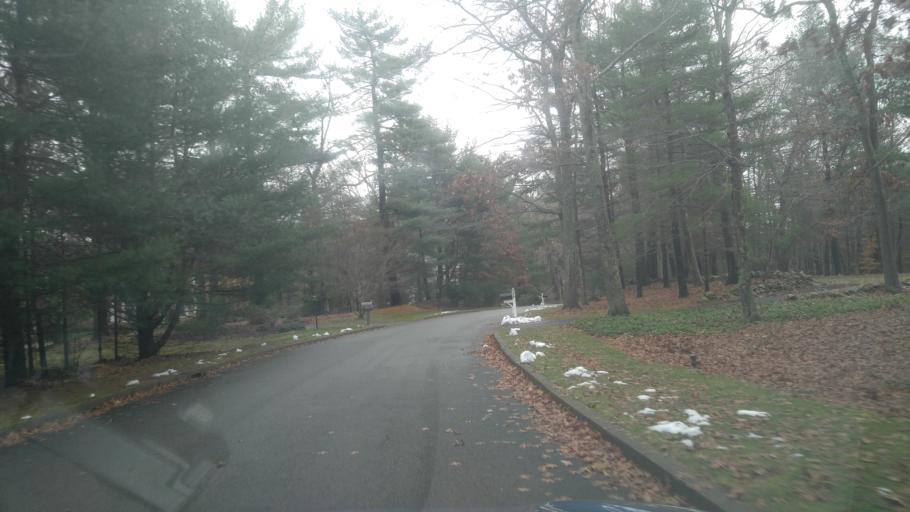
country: US
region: Rhode Island
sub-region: Kent County
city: West Warwick
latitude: 41.6487
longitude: -71.5335
